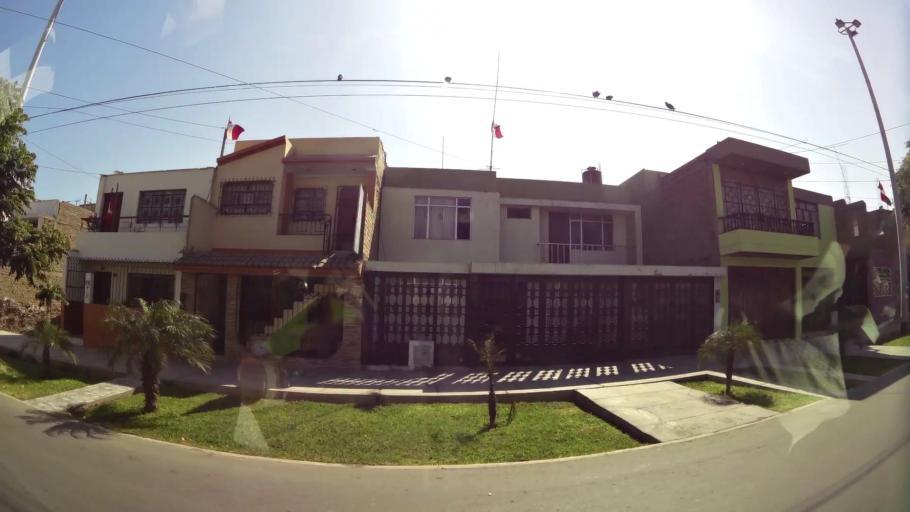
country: PE
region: Ica
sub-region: Provincia de Chincha
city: Chincha Alta
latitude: -13.4112
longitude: -76.1299
